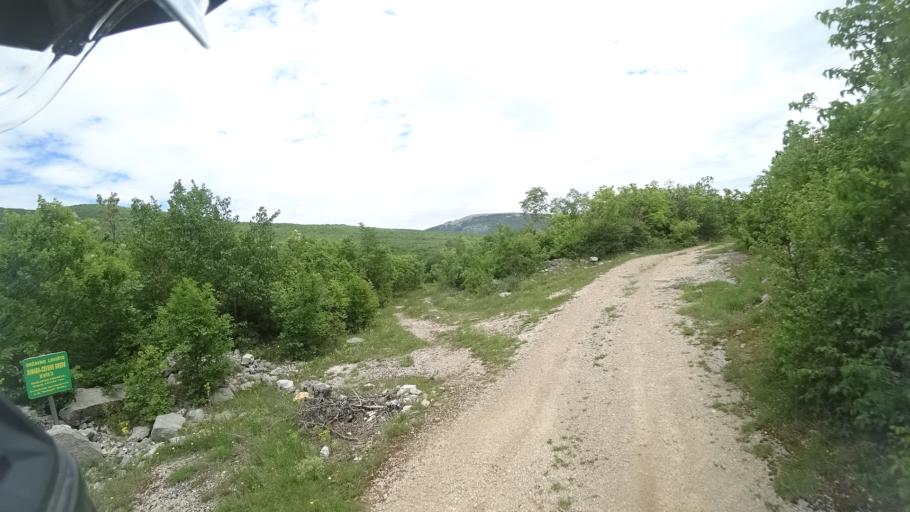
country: HR
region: Splitsko-Dalmatinska
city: Hrvace
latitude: 43.8935
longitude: 16.5495
